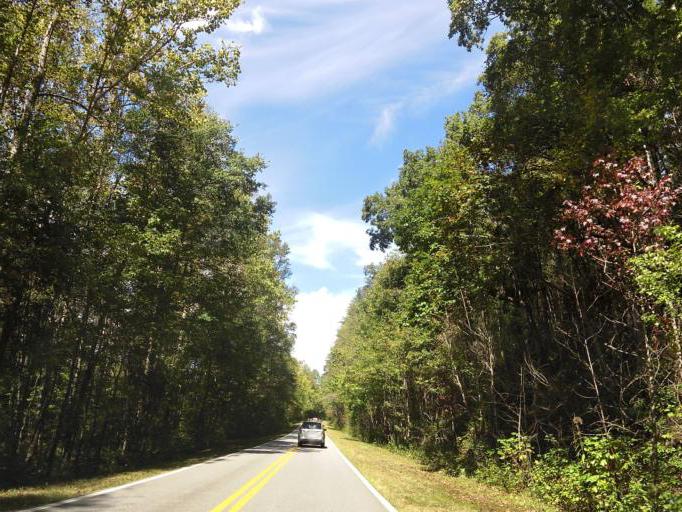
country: US
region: Georgia
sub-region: Pickens County
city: Nelson
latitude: 34.5047
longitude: -84.2757
